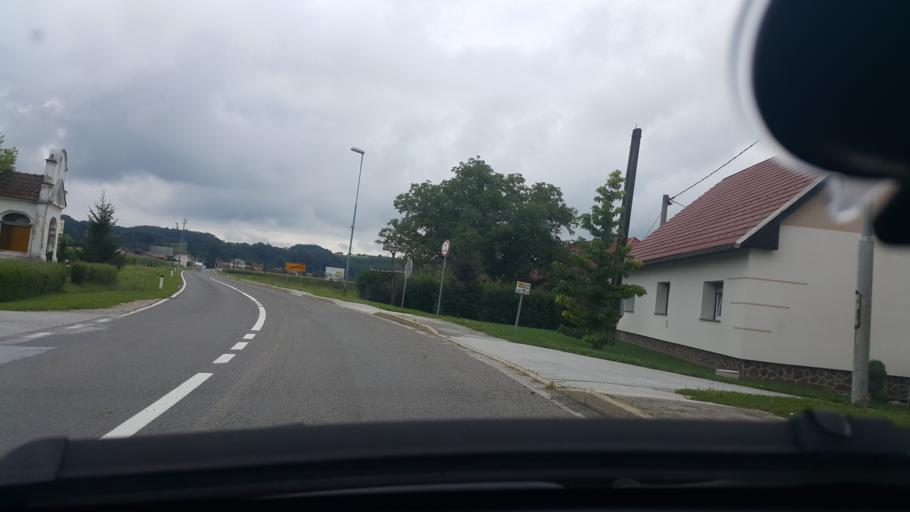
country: SI
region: Zavrc
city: Zavrc
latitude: 46.4138
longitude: 16.0986
